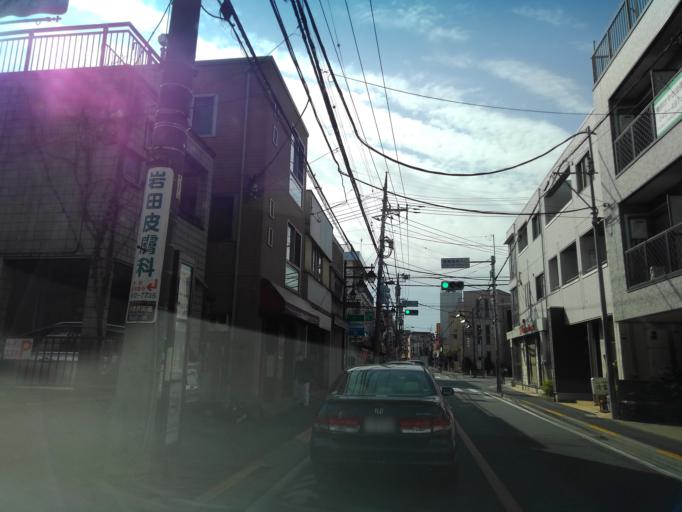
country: JP
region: Tokyo
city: Tanashicho
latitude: 35.7696
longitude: 139.5167
